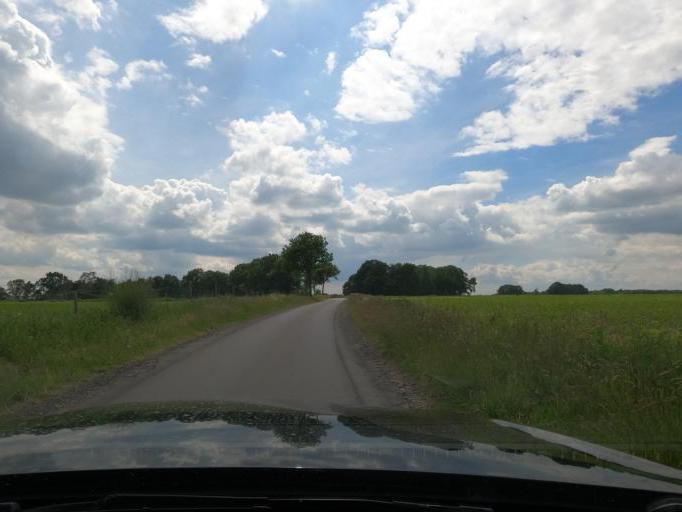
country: DE
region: Lower Saxony
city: Steimbke
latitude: 52.6414
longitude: 9.4273
